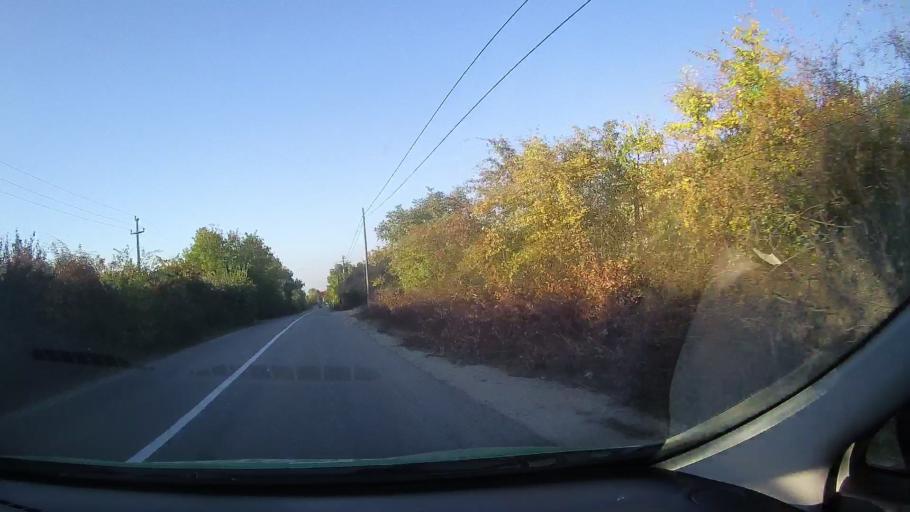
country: RO
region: Bihor
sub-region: Comuna Paleu
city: Paleu
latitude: 47.1052
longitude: 21.9286
